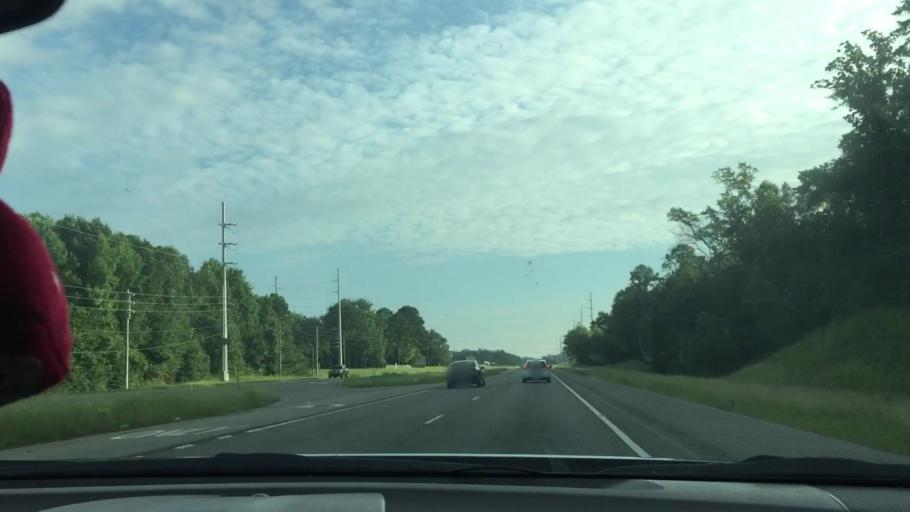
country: US
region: Alabama
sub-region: Hale County
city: Moundville
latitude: 33.0591
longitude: -87.5768
